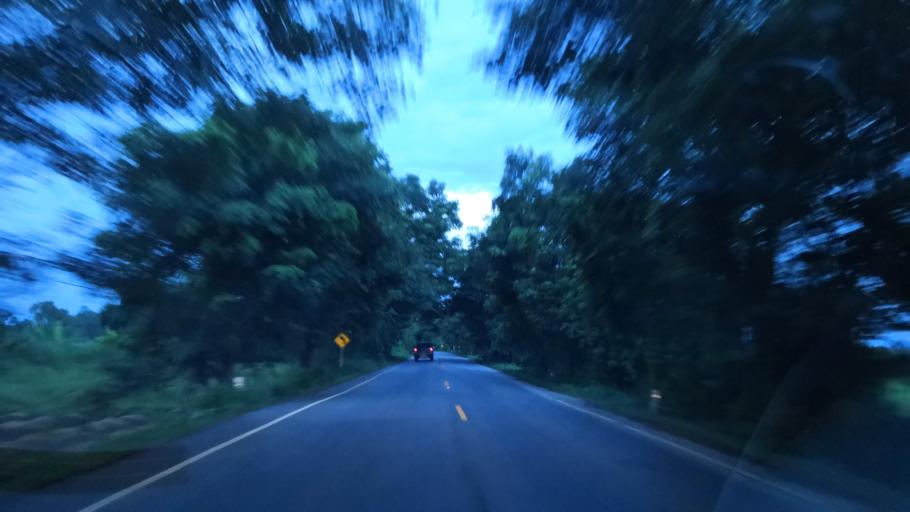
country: TH
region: Chiang Rai
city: Wiang Chai
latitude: 19.9655
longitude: 99.9625
